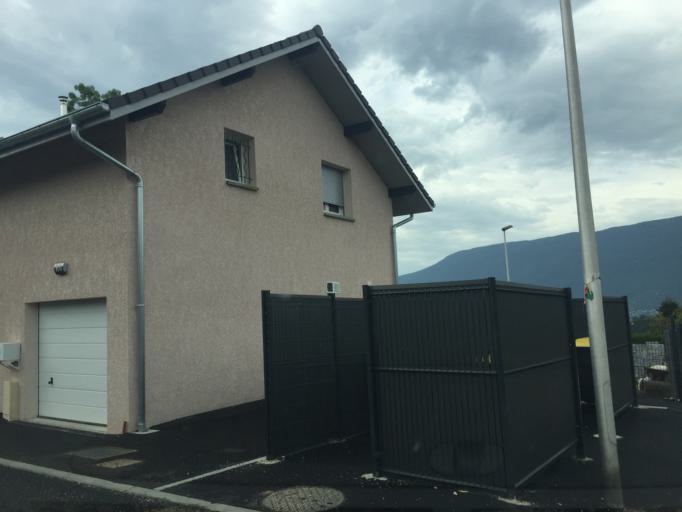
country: FR
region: Rhone-Alpes
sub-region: Departement de la Savoie
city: Aix-les-Bains
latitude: 45.6744
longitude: 5.9194
